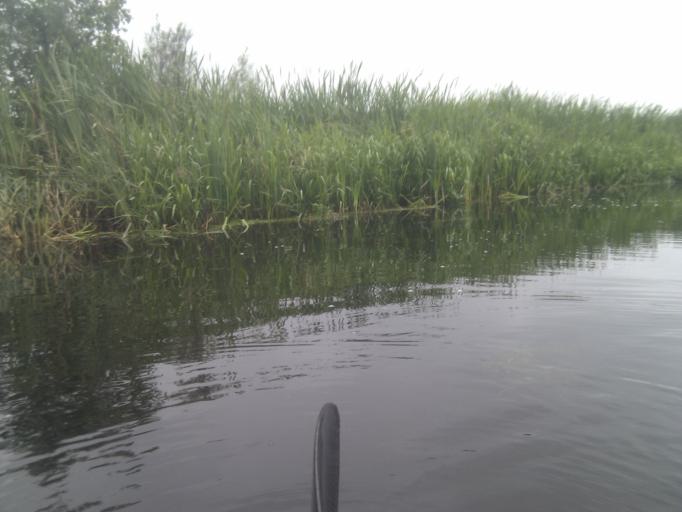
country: NL
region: Utrecht
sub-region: Gemeente De Bilt
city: De Bilt
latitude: 52.0956
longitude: 5.1980
